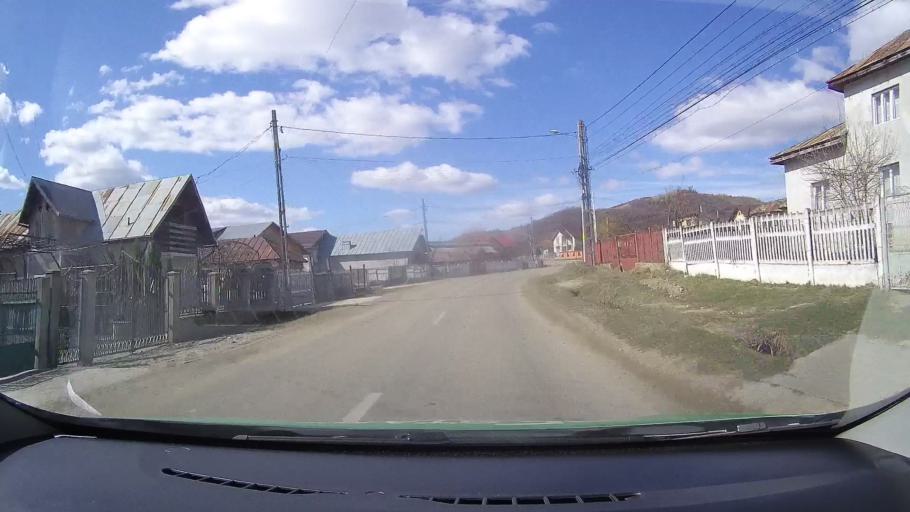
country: RO
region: Dambovita
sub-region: Comuna Glodeni
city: Glodeni
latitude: 45.0206
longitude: 25.4513
